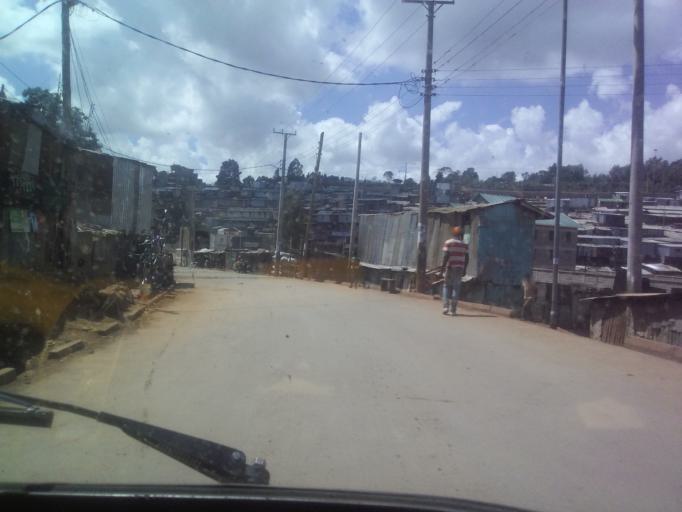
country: KE
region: Nairobi Area
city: Nairobi
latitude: -1.3151
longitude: 36.7752
